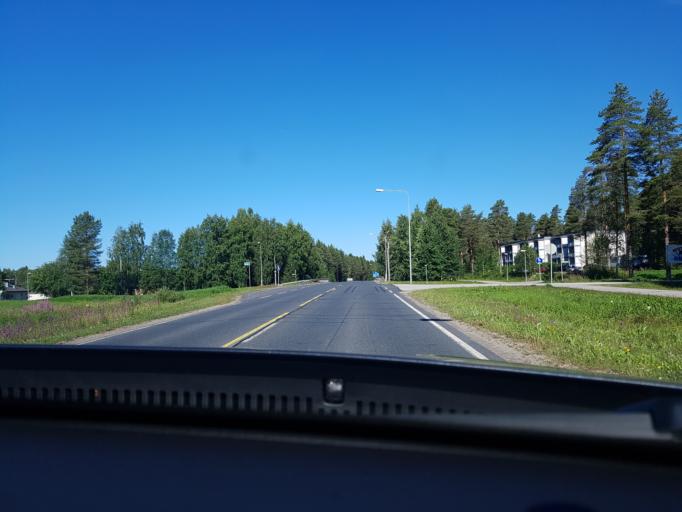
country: FI
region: Kainuu
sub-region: Kehys-Kainuu
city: Kuhmo
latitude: 64.1203
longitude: 29.5180
